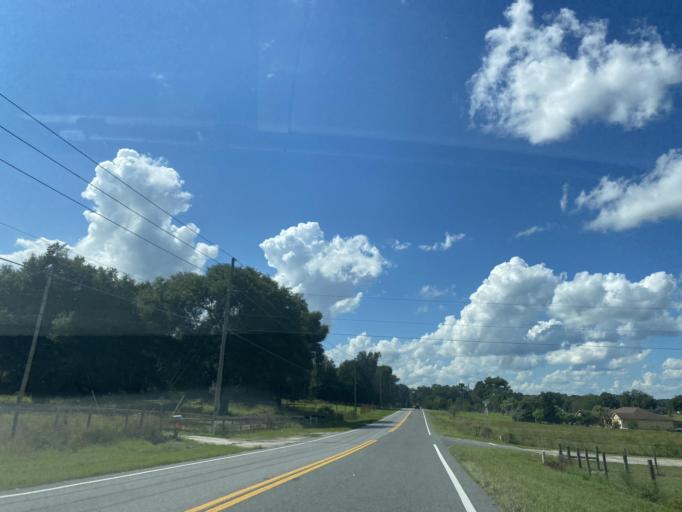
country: US
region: Florida
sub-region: Lake County
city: Lady Lake
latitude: 28.9815
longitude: -81.8832
